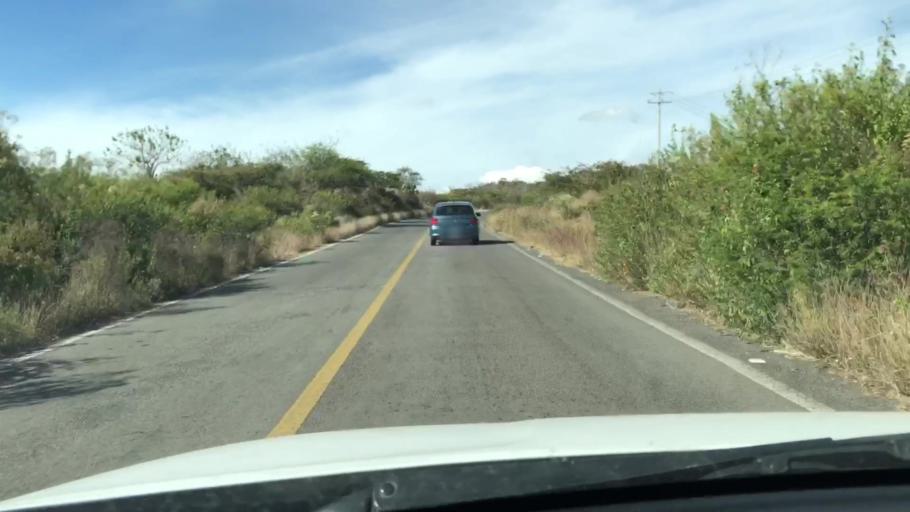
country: MX
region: Jalisco
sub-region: Zacoalco de Torres
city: Barranca de Otates (Barranca de Otatan)
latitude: 20.2105
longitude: -103.6945
